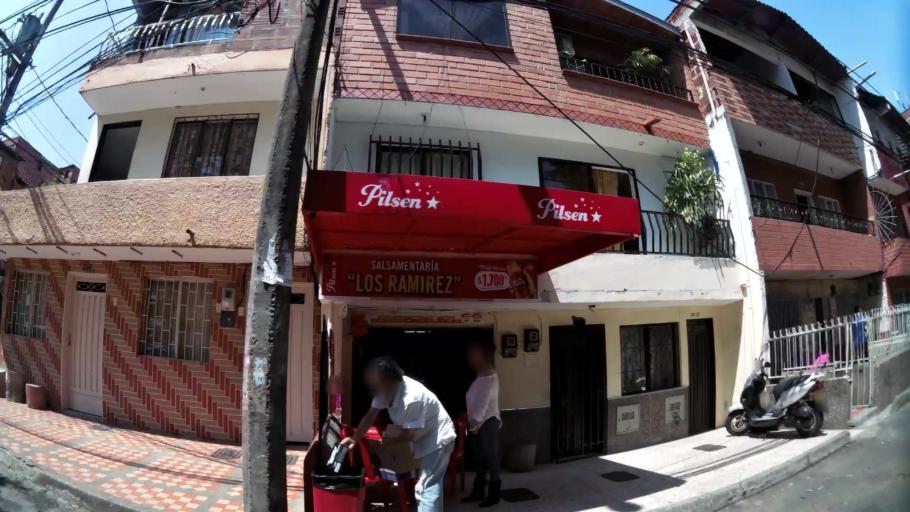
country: CO
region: Antioquia
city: Itagui
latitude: 6.2134
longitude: -75.5998
